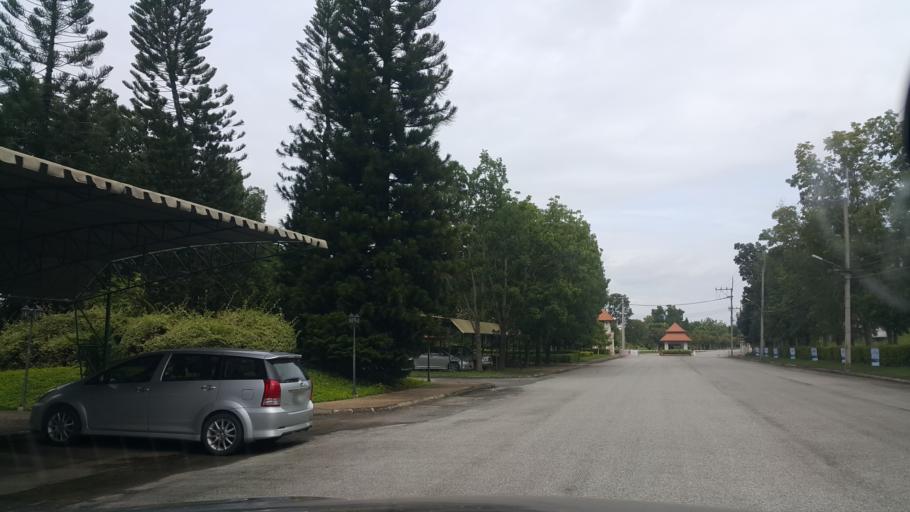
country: TH
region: Chiang Mai
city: San Kamphaeng
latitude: 18.7147
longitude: 99.1393
